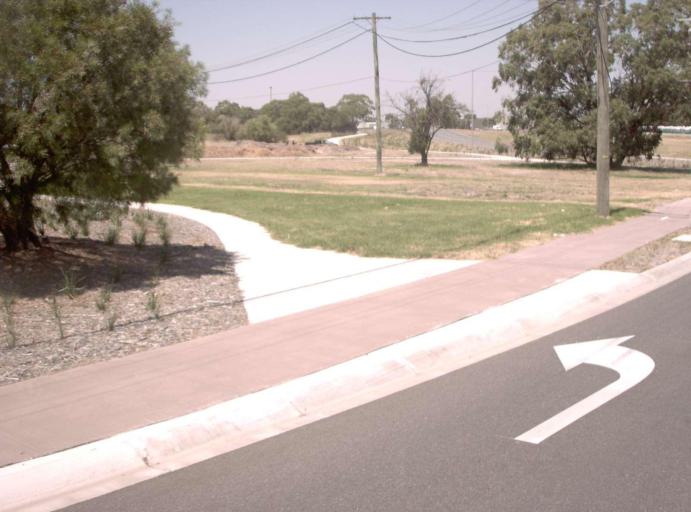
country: AU
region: Victoria
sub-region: Kingston
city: Dingley Village
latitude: -37.9818
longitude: 145.1464
